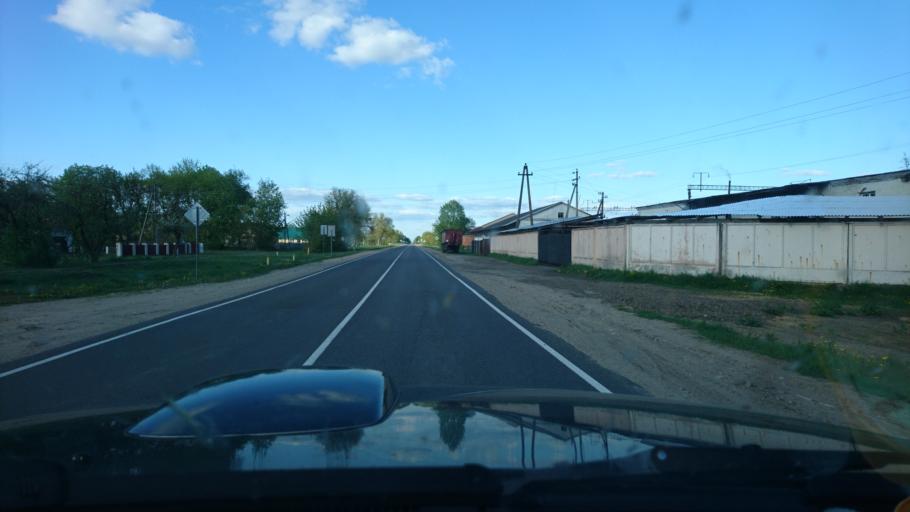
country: BY
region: Brest
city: Nyakhachava
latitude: 52.6466
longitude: 25.2109
